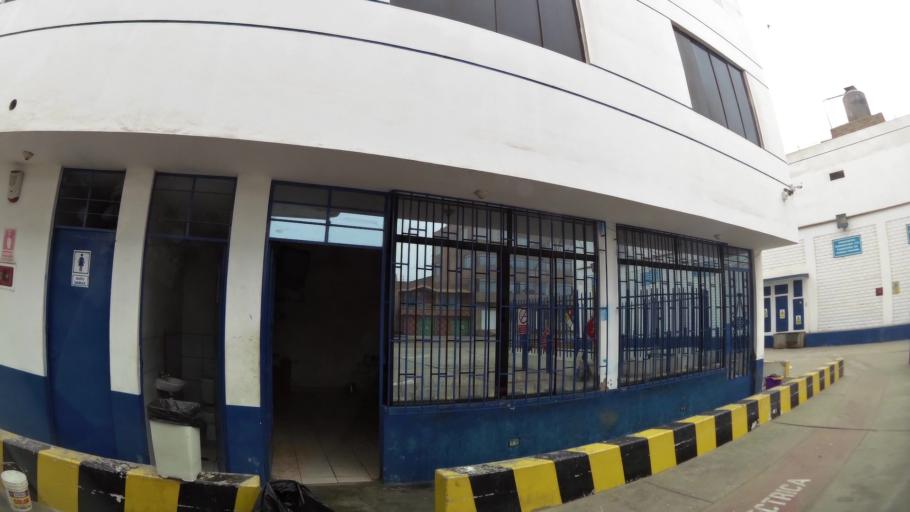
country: PE
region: Lima
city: Ventanilla
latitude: -11.8368
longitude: -77.0981
